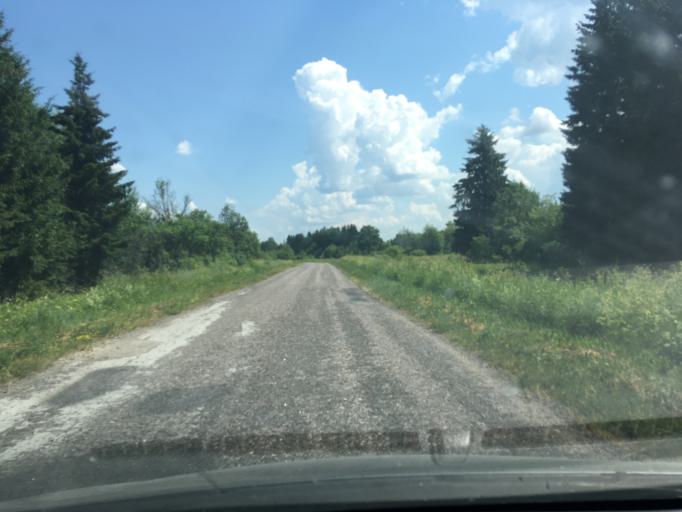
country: EE
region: Laeaene
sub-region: Lihula vald
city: Lihula
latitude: 58.6666
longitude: 23.7571
